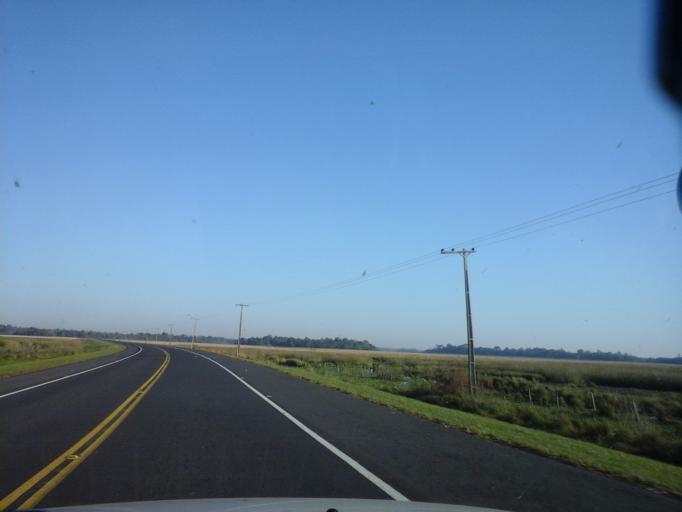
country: PY
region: Neembucu
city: Pilar
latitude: -26.8625
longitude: -57.9445
